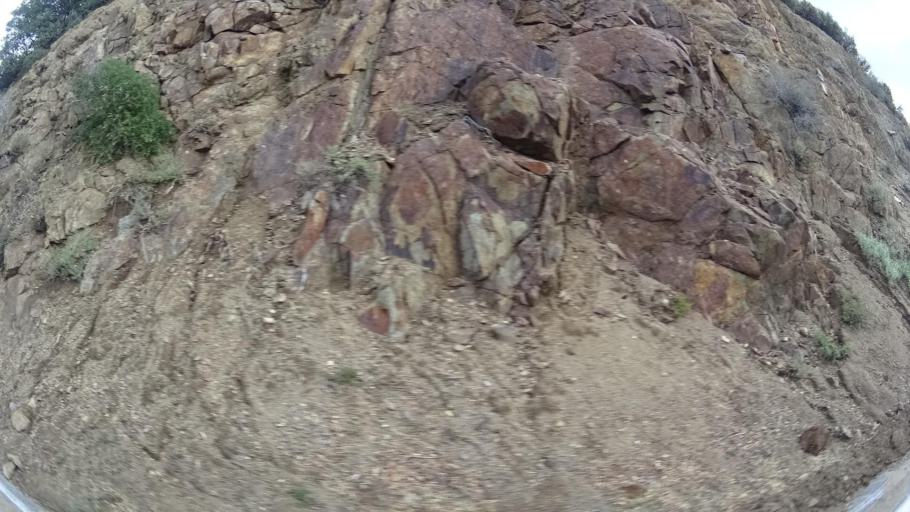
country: US
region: California
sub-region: San Diego County
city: Pine Valley
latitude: 32.8376
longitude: -116.4962
